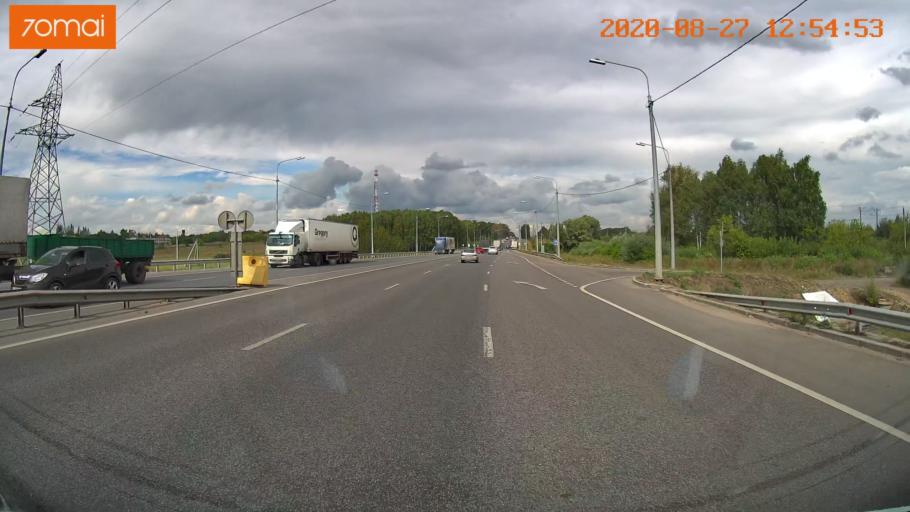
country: RU
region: Rjazan
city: Ryazan'
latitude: 54.6165
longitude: 39.6372
